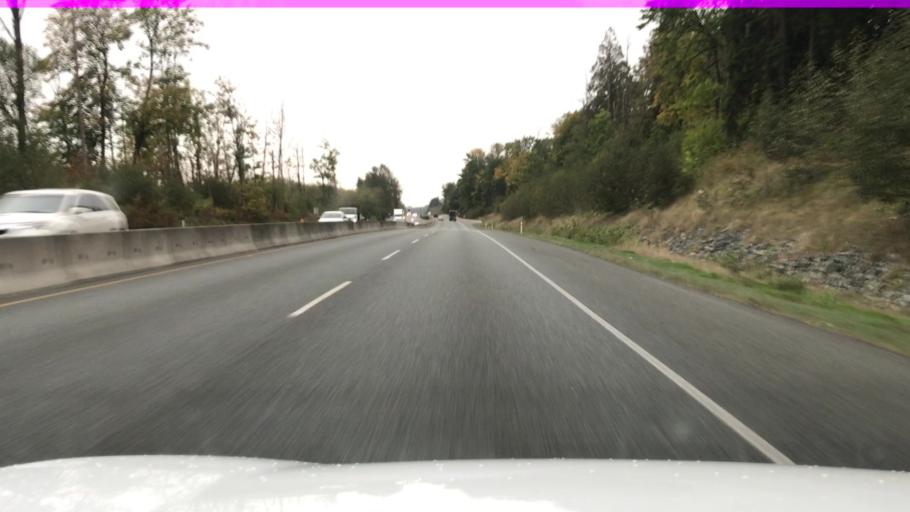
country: CA
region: British Columbia
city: Pitt Meadows
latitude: 49.2064
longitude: -122.7633
